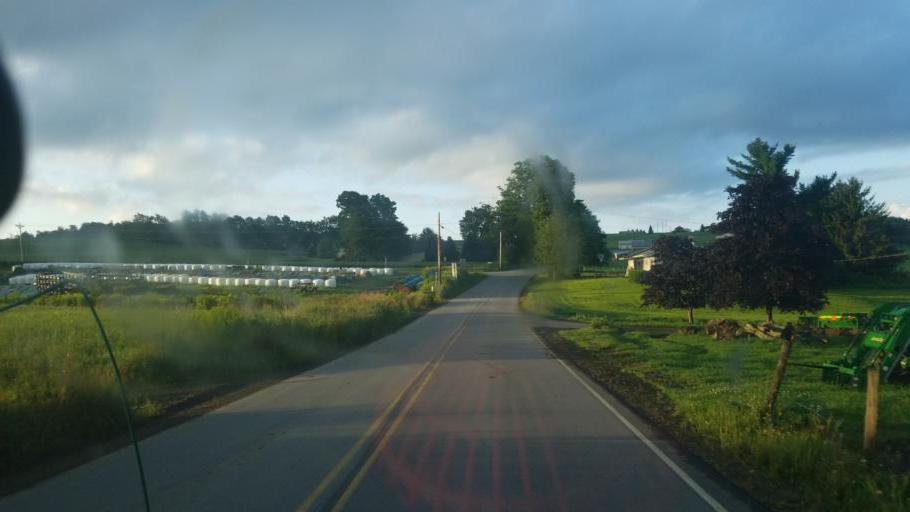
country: US
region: Pennsylvania
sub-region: Potter County
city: Galeton
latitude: 41.8879
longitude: -77.7614
